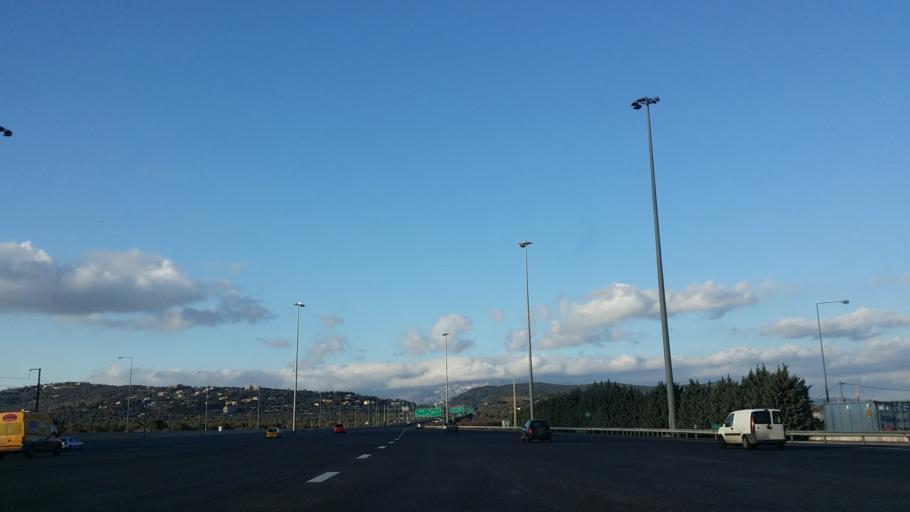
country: GR
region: Attica
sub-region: Nomarchia Anatolikis Attikis
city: Karellas
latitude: 37.9386
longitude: 23.8869
